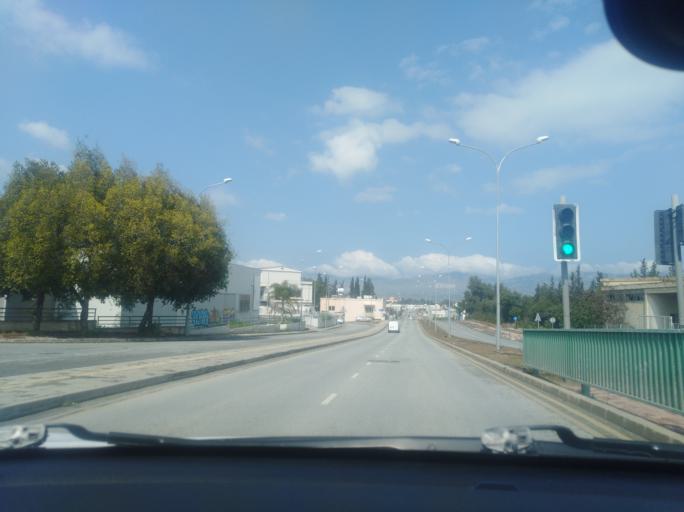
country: CY
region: Lefkosia
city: Nicosia
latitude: 35.1758
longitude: 33.3961
